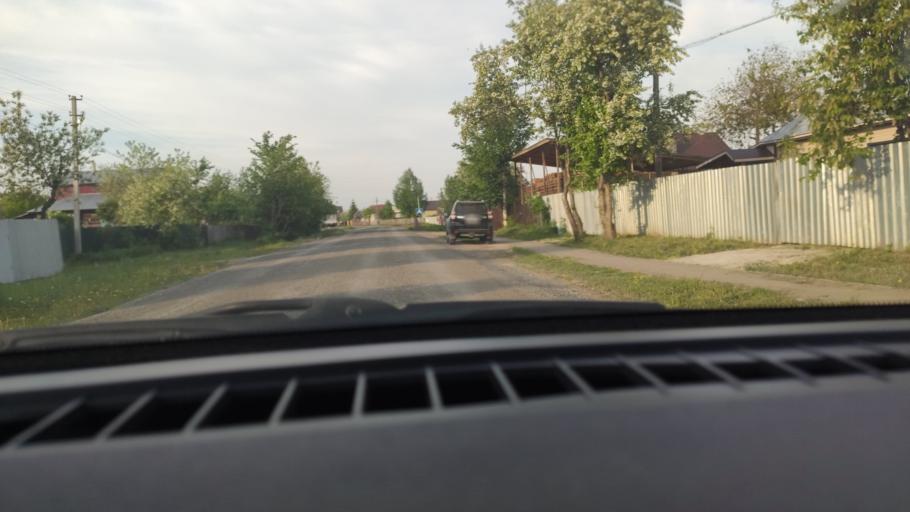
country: RU
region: Perm
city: Kondratovo
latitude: 57.9356
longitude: 56.0248
